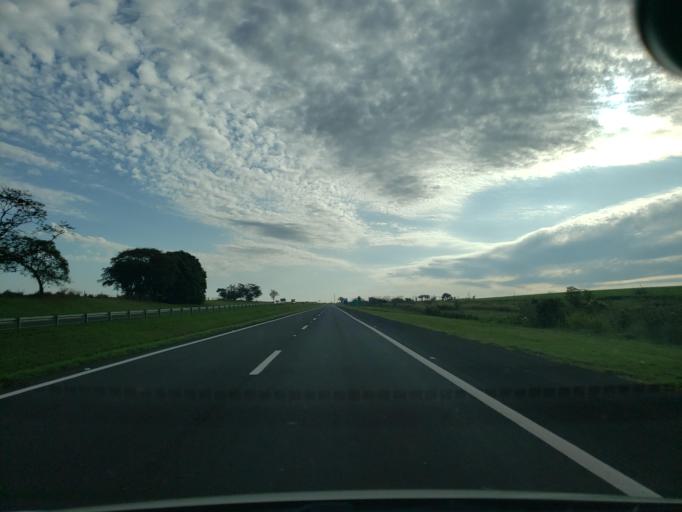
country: BR
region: Sao Paulo
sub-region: Guararapes
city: Guararapes
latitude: -21.2088
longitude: -50.7442
